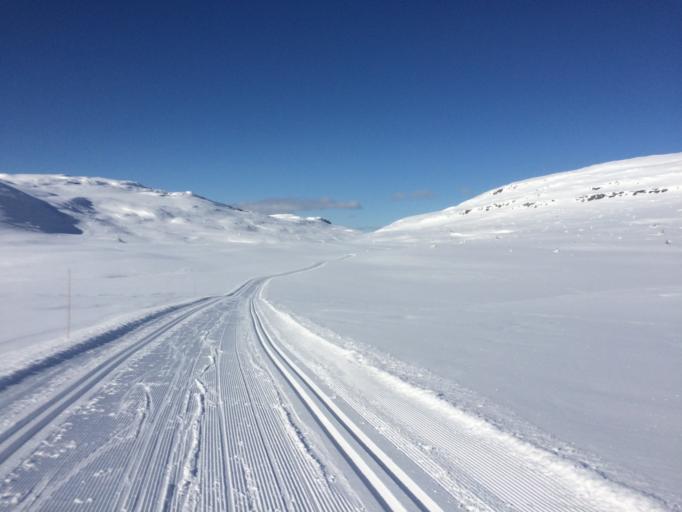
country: NO
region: Oppland
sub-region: Ringebu
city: Ringebu
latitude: 61.3791
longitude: 10.0611
